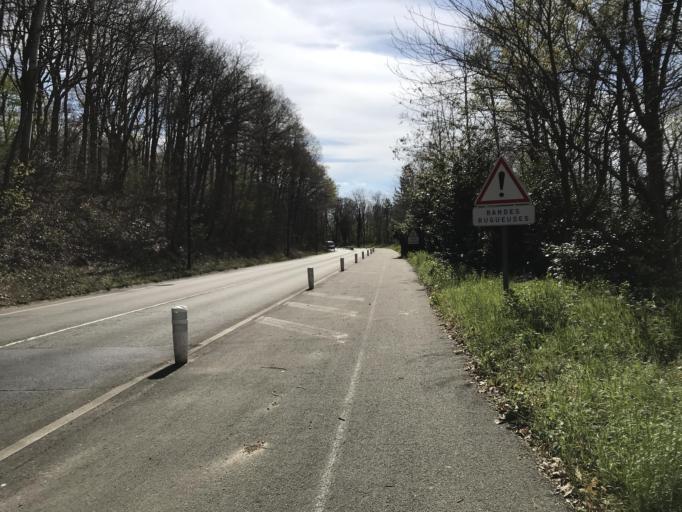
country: FR
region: Ile-de-France
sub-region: Departement de l'Essonne
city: Les Ulis
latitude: 48.6903
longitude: 2.1628
